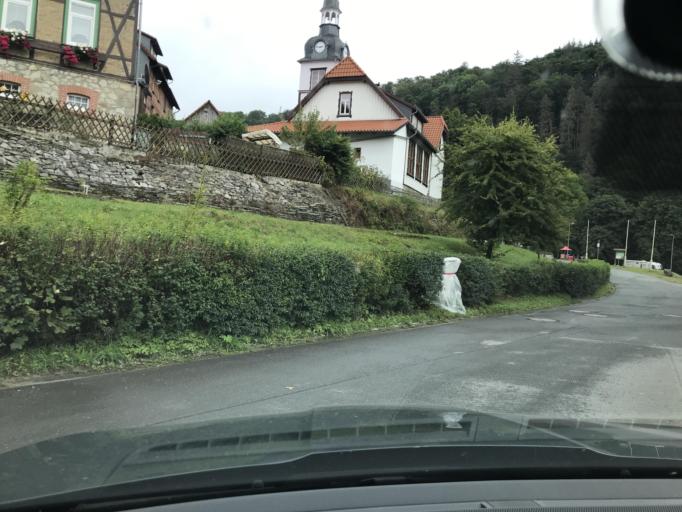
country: DE
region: Saxony-Anhalt
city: Rubeland
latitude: 51.7528
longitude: 10.8745
